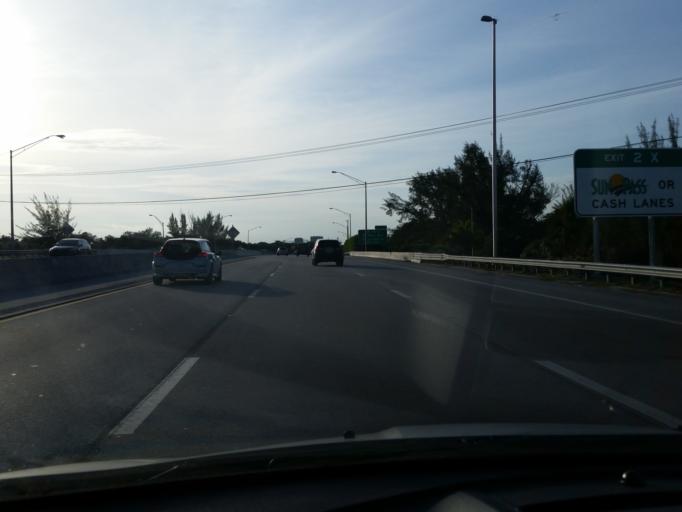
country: US
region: Florida
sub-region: Miami-Dade County
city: Scott Lake
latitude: 25.9411
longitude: -80.2219
